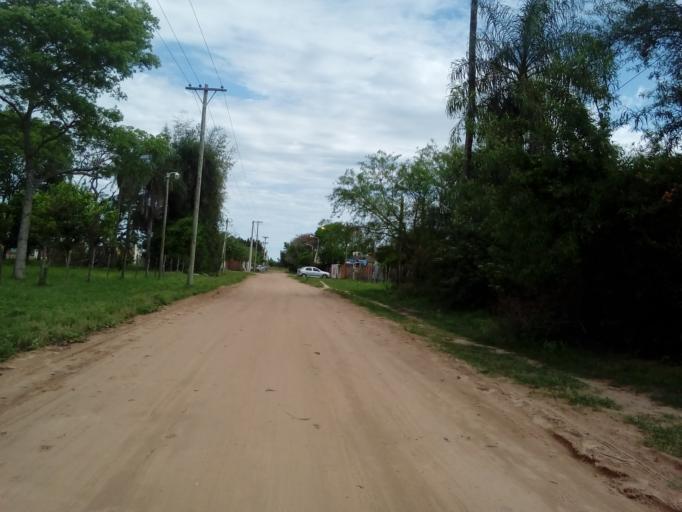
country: AR
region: Corrientes
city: San Luis del Palmar
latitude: -27.4609
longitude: -58.6526
